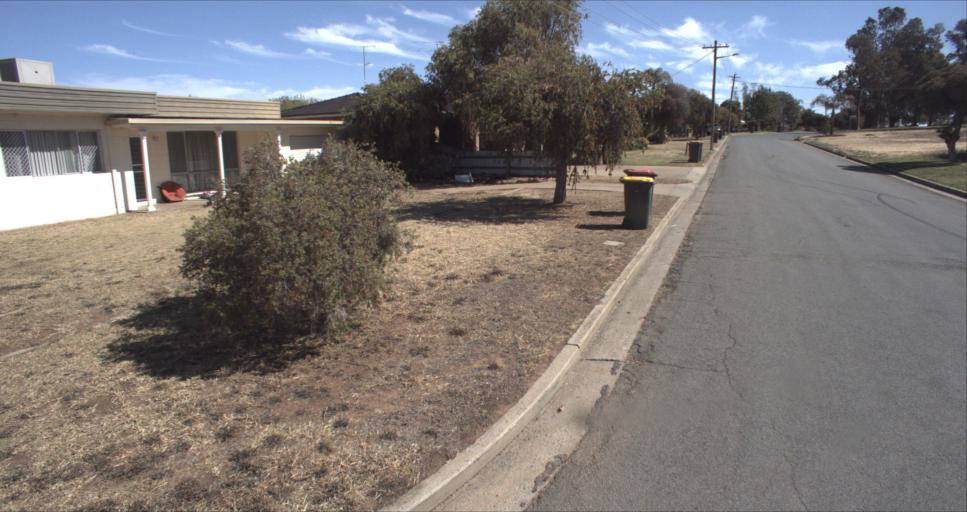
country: AU
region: New South Wales
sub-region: Leeton
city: Leeton
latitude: -34.5509
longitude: 146.3790
